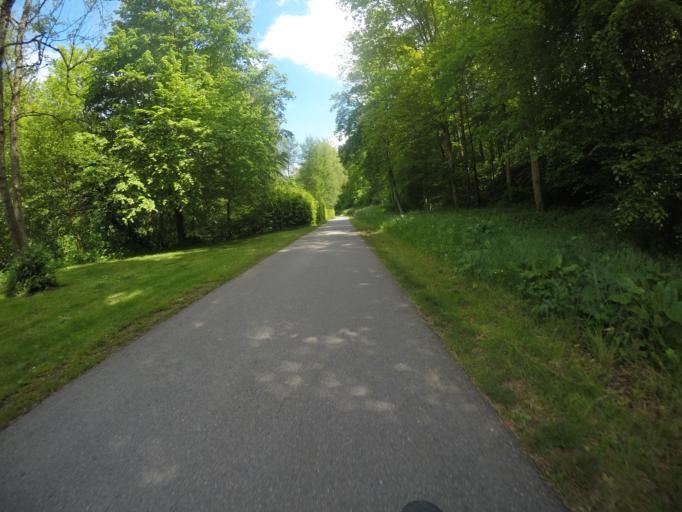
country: DE
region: Baden-Wuerttemberg
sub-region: Karlsruhe Region
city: Wildberg
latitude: 48.6152
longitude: 8.7403
